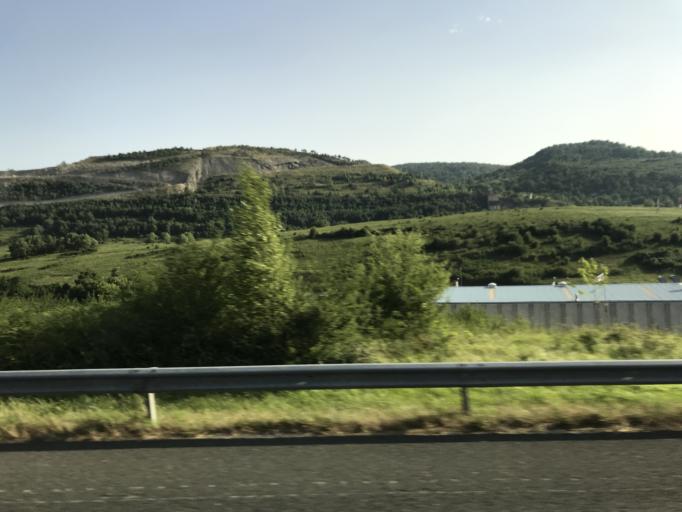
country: ES
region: Navarre
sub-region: Provincia de Navarra
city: Altsasu
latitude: 42.9152
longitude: -2.1865
